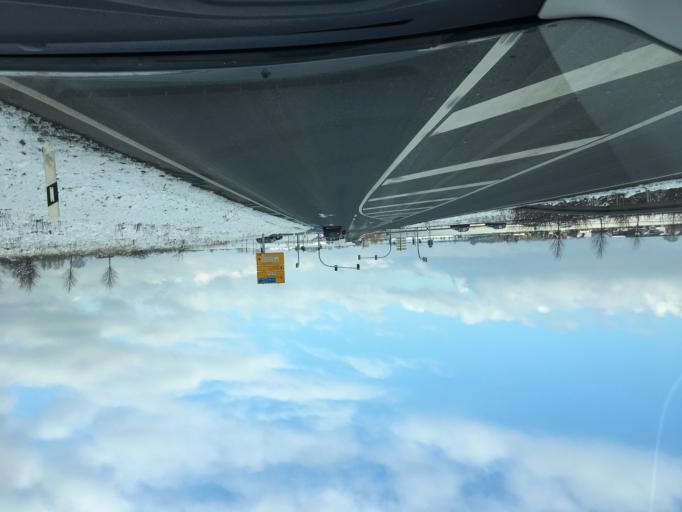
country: DE
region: Saxony
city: Grimma
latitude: 51.2308
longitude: 12.6973
